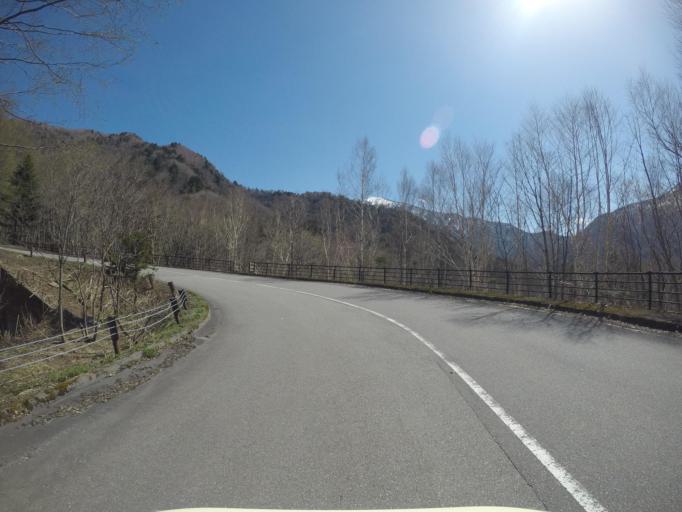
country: JP
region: Gifu
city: Takayama
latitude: 36.1944
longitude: 137.5576
